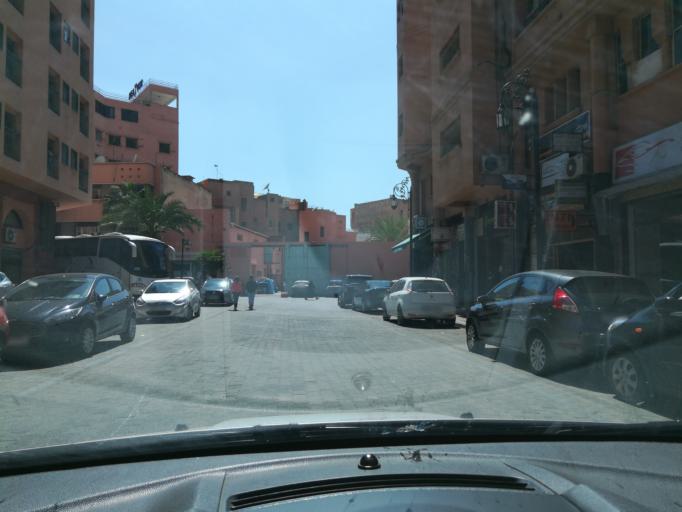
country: MA
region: Marrakech-Tensift-Al Haouz
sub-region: Marrakech
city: Marrakesh
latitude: 31.6371
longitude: -8.0143
